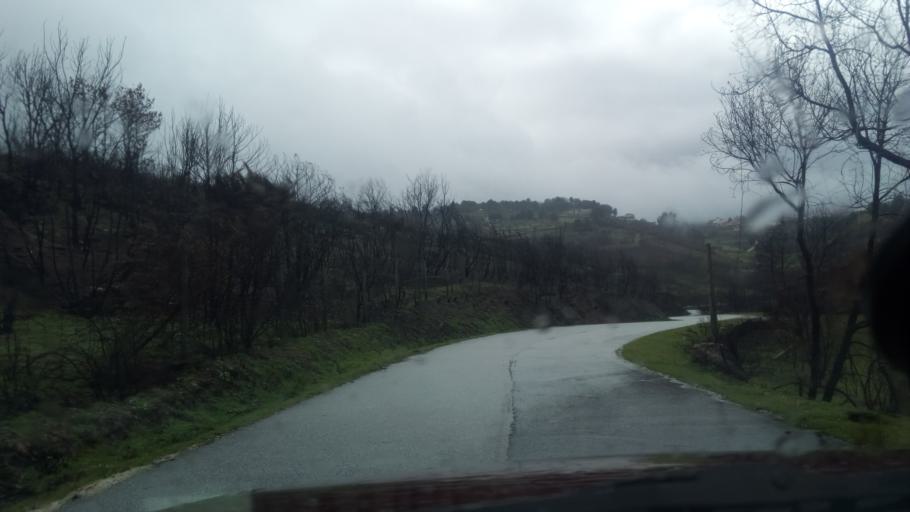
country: PT
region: Guarda
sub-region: Fornos de Algodres
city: Fornos de Algodres
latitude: 40.5500
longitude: -7.4773
